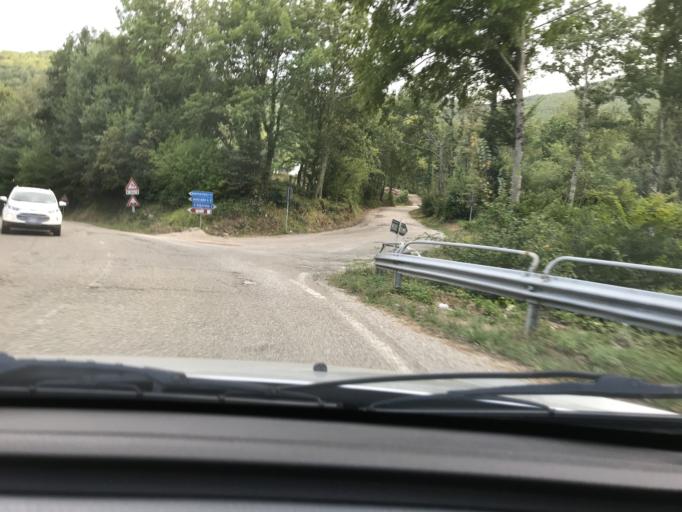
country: IT
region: Umbria
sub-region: Provincia di Terni
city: Guardea
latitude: 42.6484
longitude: 12.3521
